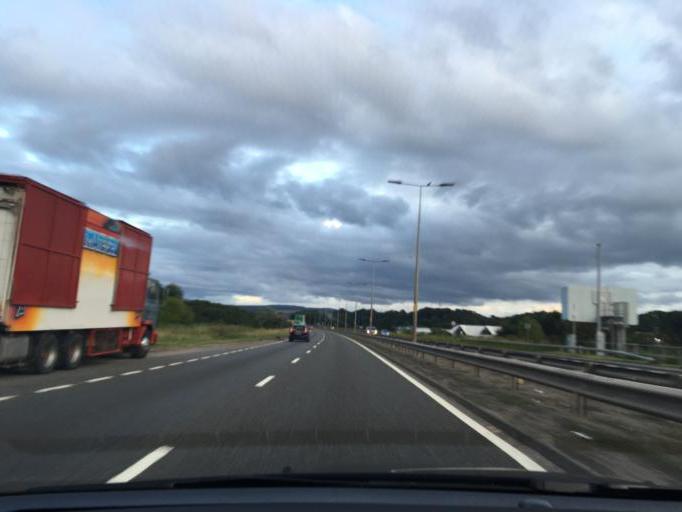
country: GB
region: Scotland
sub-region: Highland
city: Inverness
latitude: 57.4876
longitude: -4.2080
